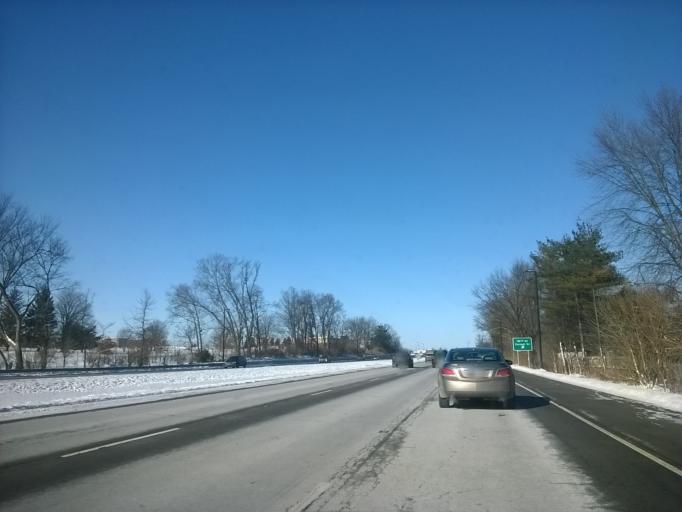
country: US
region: Indiana
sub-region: Hamilton County
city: Carmel
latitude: 39.9520
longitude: -86.1136
